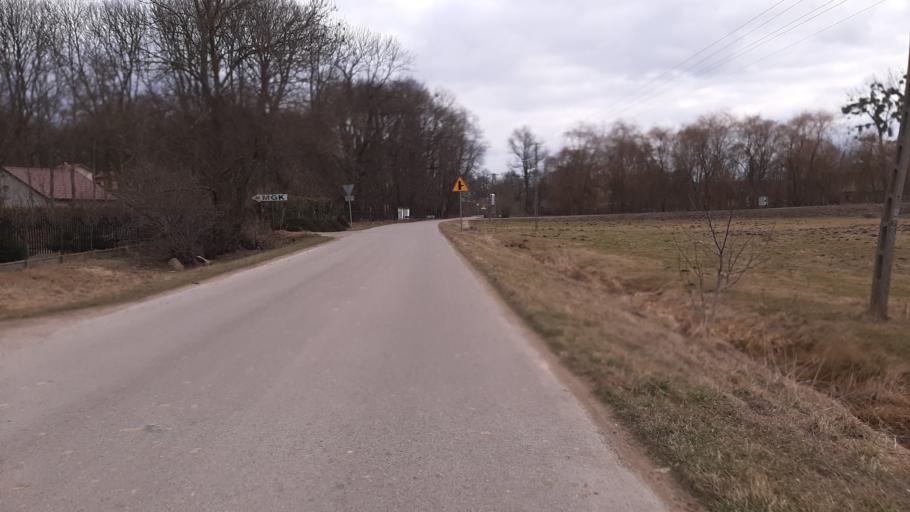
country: PL
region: Lublin Voivodeship
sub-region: Powiat lubelski
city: Jastkow
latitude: 51.3431
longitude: 22.4121
